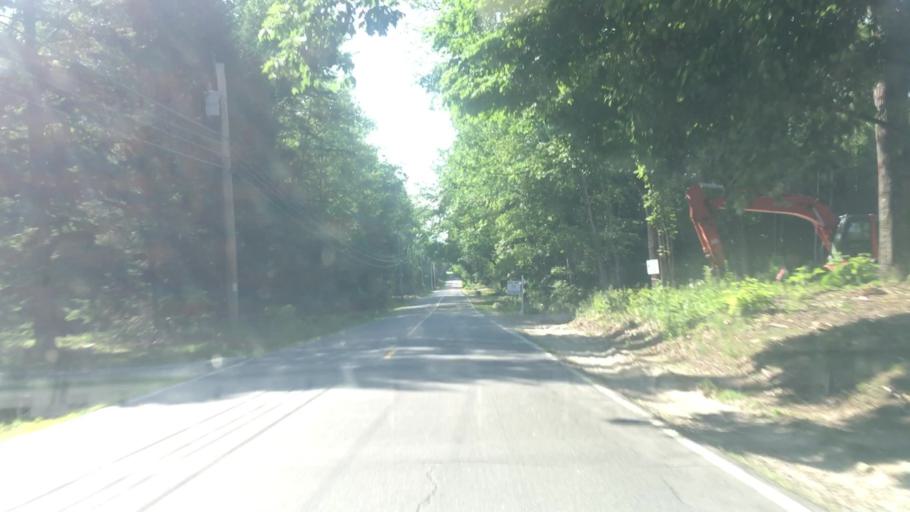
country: US
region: Maine
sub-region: York County
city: Hollis Center
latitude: 43.6370
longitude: -70.5771
